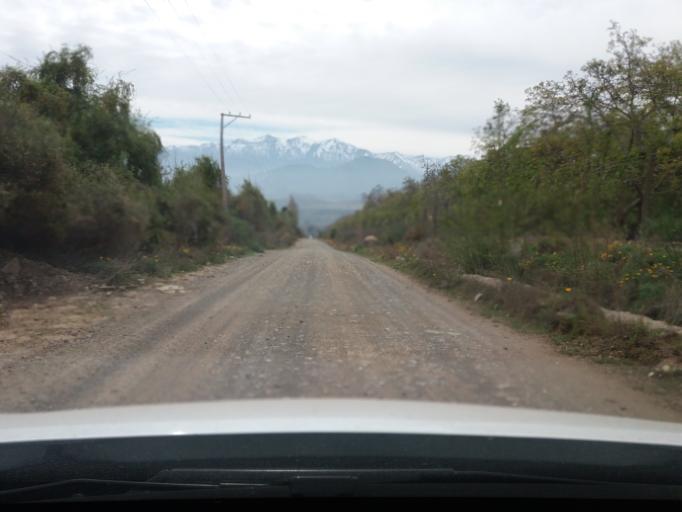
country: CL
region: Valparaiso
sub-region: Provincia de Los Andes
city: Los Andes
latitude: -32.8484
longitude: -70.5554
